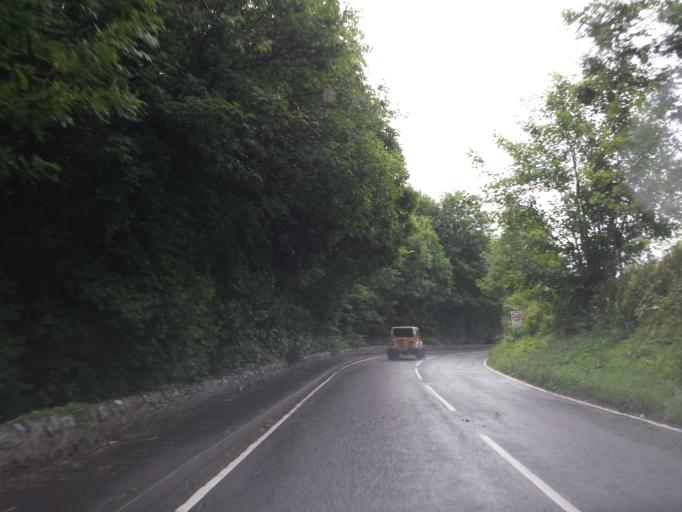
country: GB
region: Scotland
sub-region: Fife
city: Newburgh
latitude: 56.3428
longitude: -3.2132
